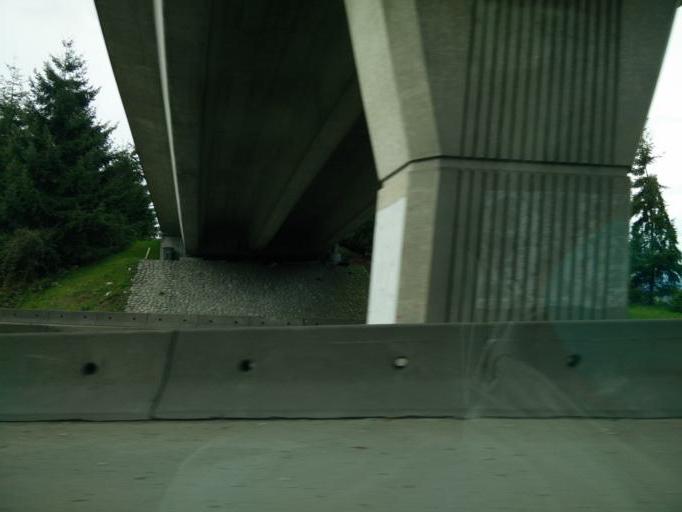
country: CA
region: British Columbia
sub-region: Fraser Valley Regional District
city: North Vancouver
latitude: 49.2871
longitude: -123.0310
